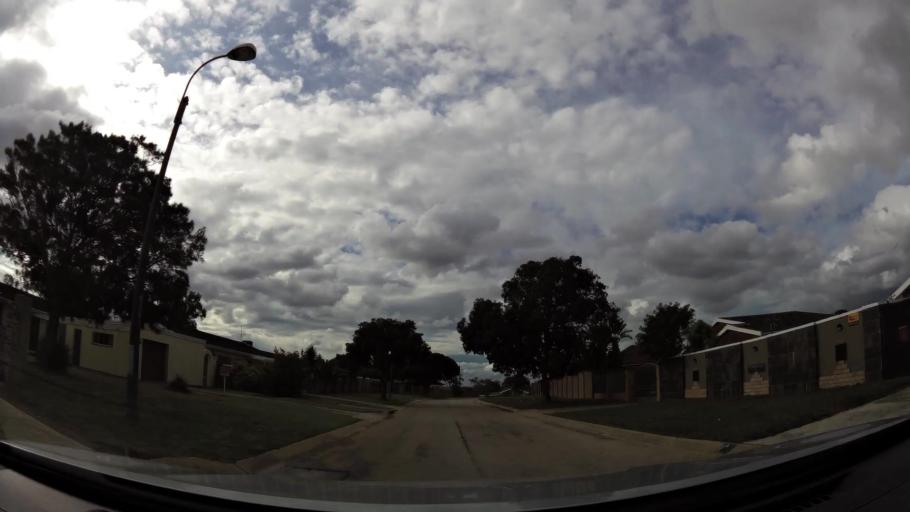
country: ZA
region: Eastern Cape
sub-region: Nelson Mandela Bay Metropolitan Municipality
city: Port Elizabeth
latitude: -33.9336
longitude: 25.5079
